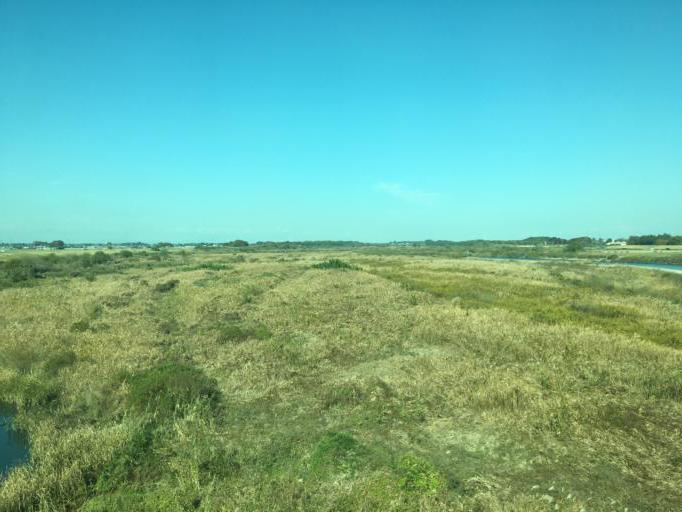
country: JP
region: Ibaraki
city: Yuki
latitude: 36.2963
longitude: 139.9077
